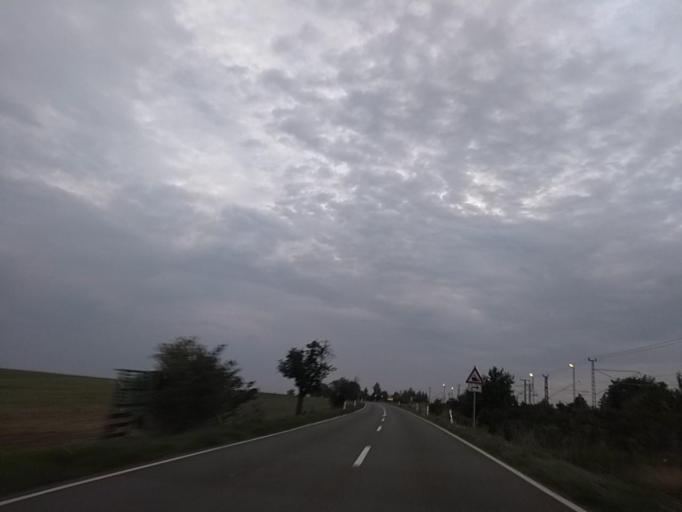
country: DE
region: Saxony-Anhalt
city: Hohenmolsen
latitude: 51.1276
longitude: 12.1486
